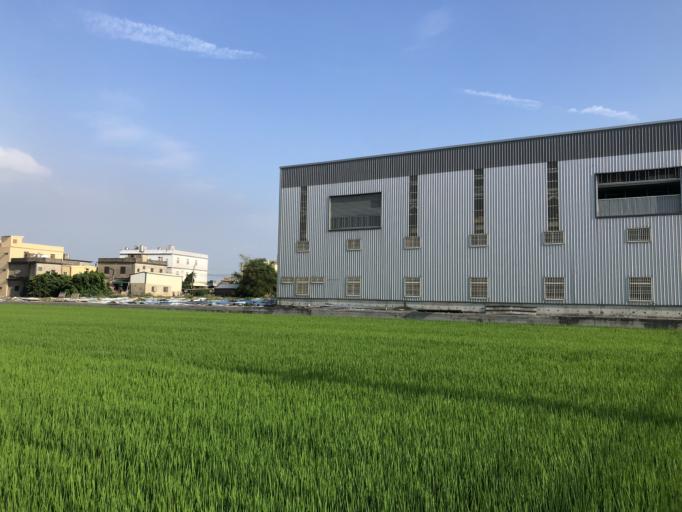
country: TW
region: Taiwan
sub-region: Changhua
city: Chang-hua
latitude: 24.0542
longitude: 120.4652
